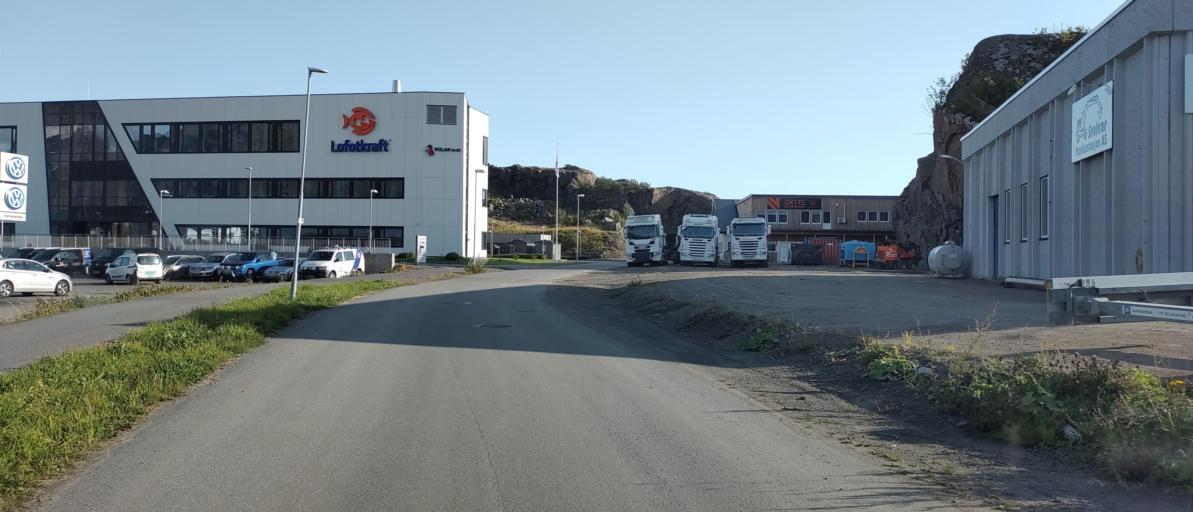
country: NO
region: Nordland
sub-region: Vagan
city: Svolvaer
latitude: 68.2260
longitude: 14.5550
